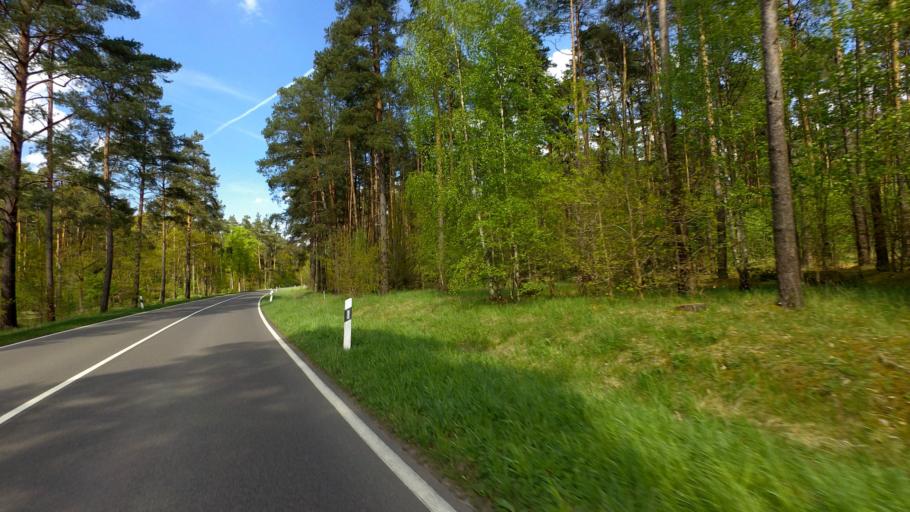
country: DE
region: Brandenburg
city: Milmersdorf
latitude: 53.0793
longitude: 13.6213
